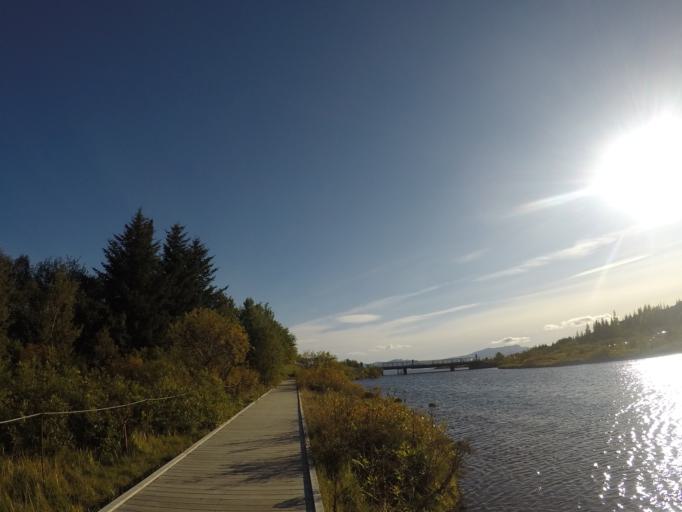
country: IS
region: South
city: Hveragerdi
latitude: 64.2568
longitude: -21.1223
